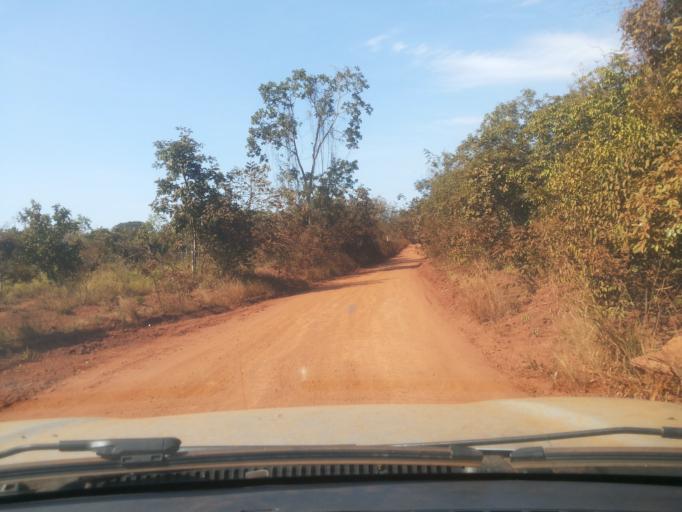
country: BR
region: Minas Gerais
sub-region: Ituiutaba
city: Ituiutaba
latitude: -19.0485
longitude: -49.3652
